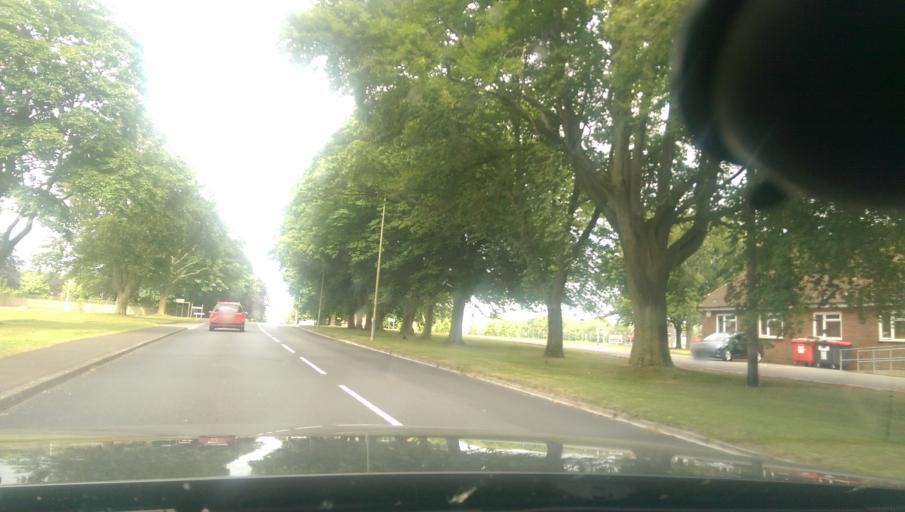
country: GB
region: England
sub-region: Wiltshire
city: Amesbury
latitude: 51.1979
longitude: -1.8203
